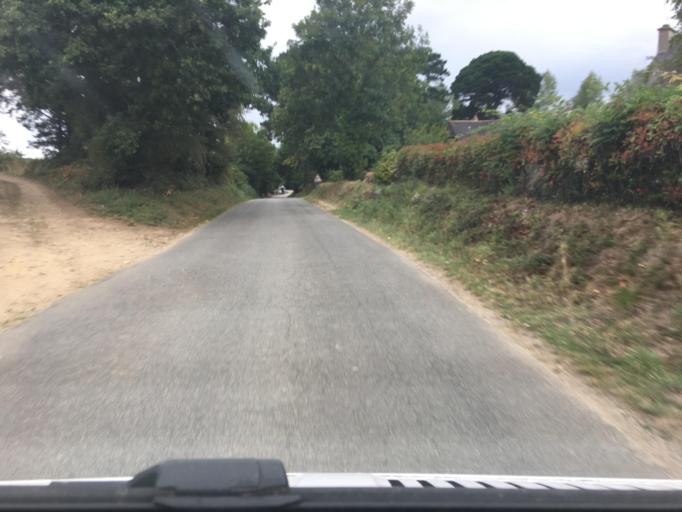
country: FR
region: Brittany
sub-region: Departement du Finistere
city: Beuzec-Cap-Sizun
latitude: 48.0781
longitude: -4.4762
